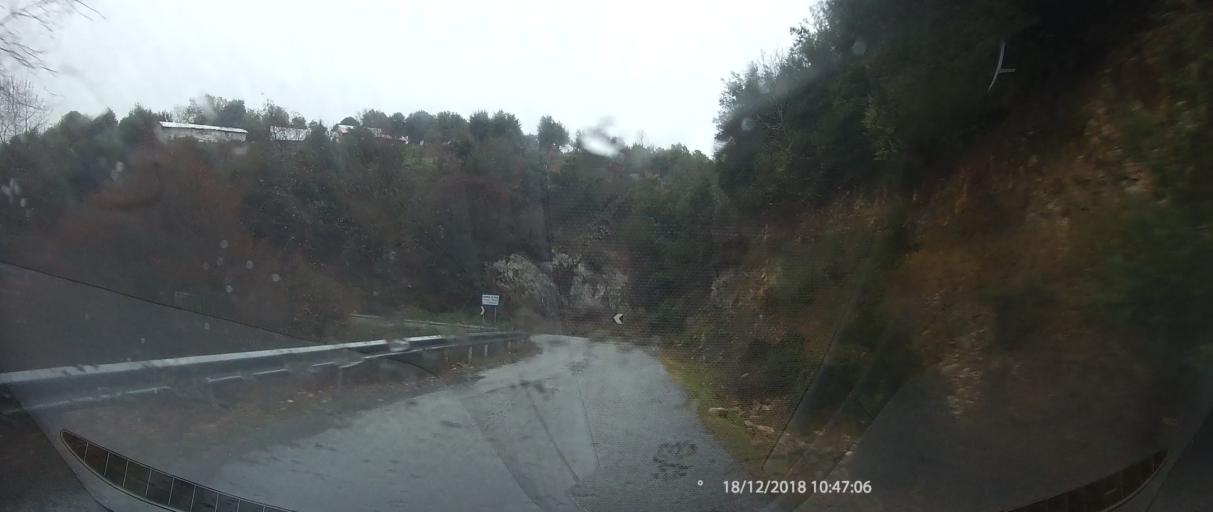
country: GR
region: Central Macedonia
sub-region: Nomos Pierias
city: Kato Milia
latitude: 40.1831
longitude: 22.3277
